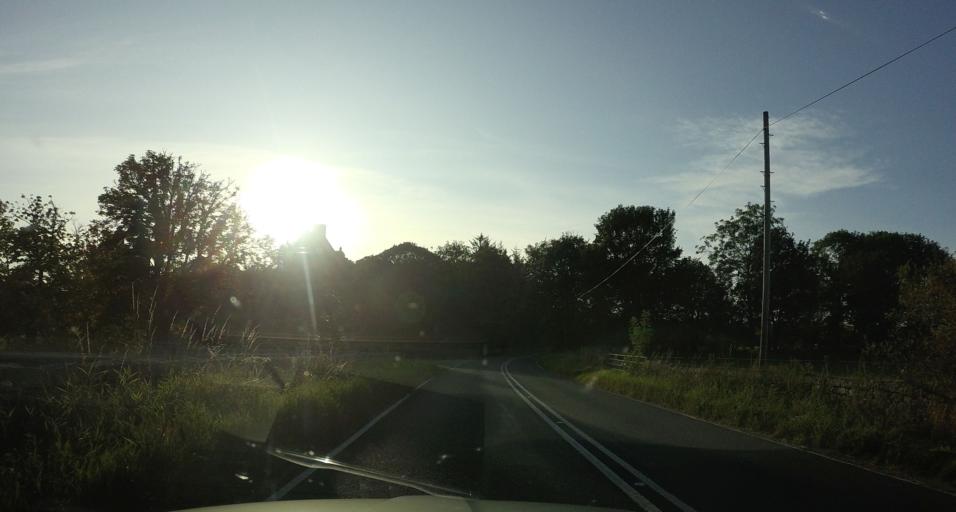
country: GB
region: Scotland
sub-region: Aberdeenshire
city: Kintore
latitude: 57.1633
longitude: -2.3550
